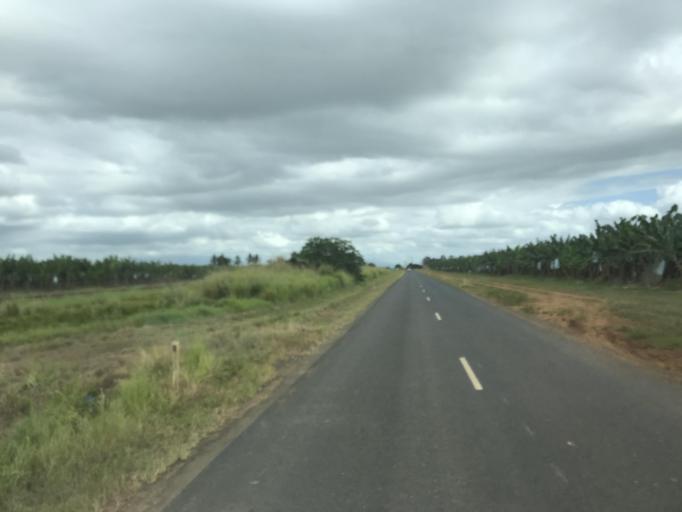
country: AU
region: Queensland
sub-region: Cassowary Coast
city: Innisfail
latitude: -17.6105
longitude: 146.0142
